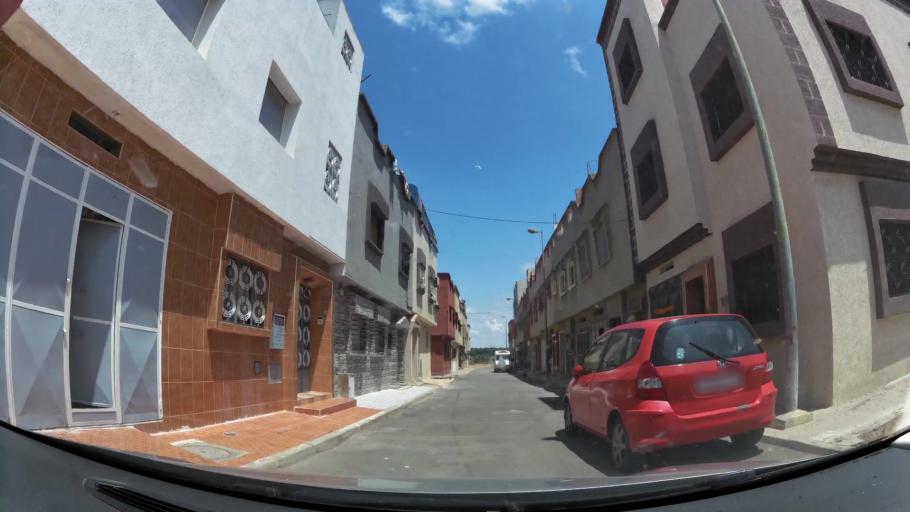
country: MA
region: Gharb-Chrarda-Beni Hssen
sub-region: Kenitra Province
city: Kenitra
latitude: 34.2640
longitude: -6.5539
